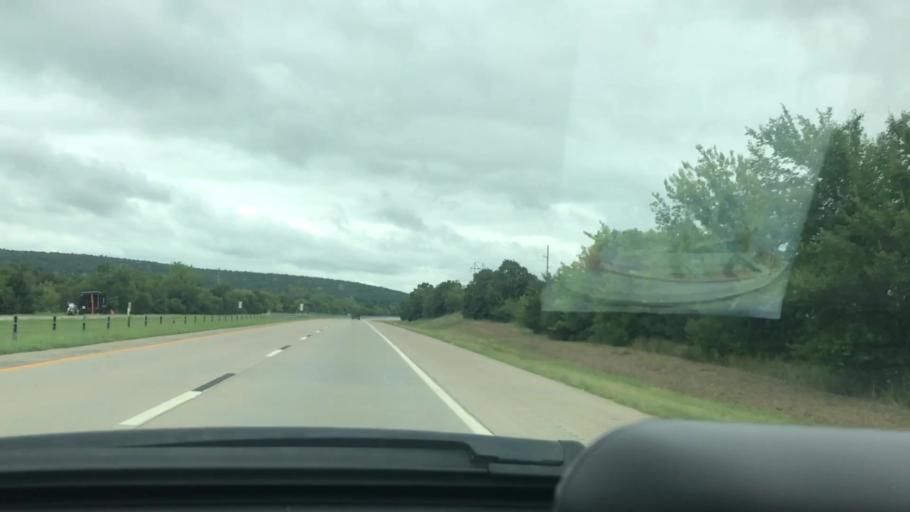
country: US
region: Oklahoma
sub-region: Pittsburg County
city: Krebs
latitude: 35.0104
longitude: -95.7187
